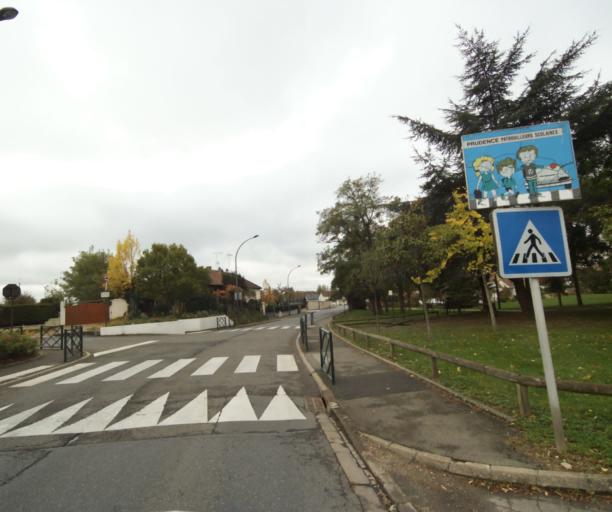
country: FR
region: Centre
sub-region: Departement d'Eure-et-Loir
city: Dreux
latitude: 48.7438
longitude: 1.3654
